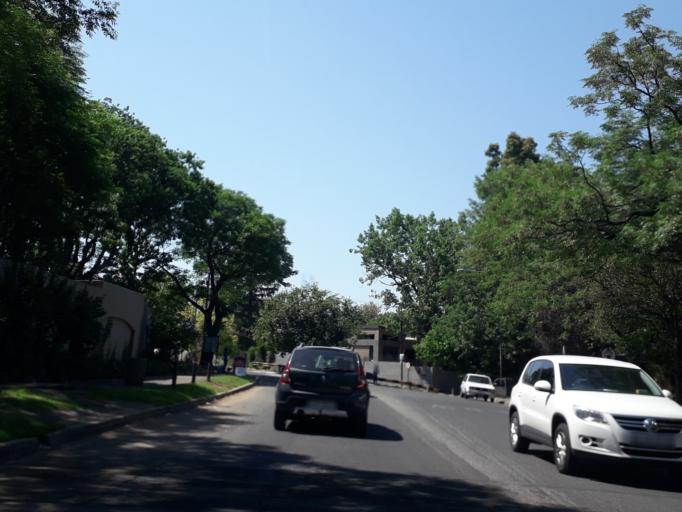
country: ZA
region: Gauteng
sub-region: City of Johannesburg Metropolitan Municipality
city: Johannesburg
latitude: -26.1311
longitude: 28.0250
